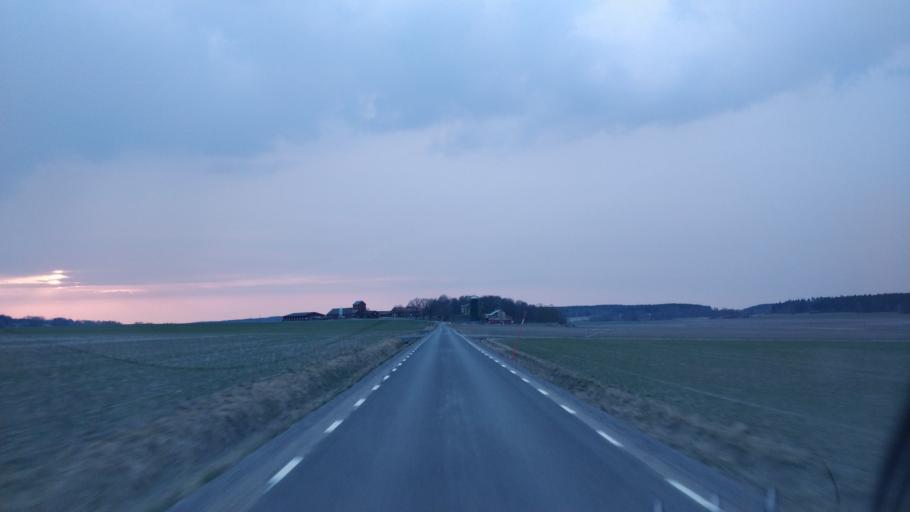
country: SE
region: Uppsala
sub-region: Enkopings Kommun
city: Orsundsbro
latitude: 59.7360
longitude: 17.1909
